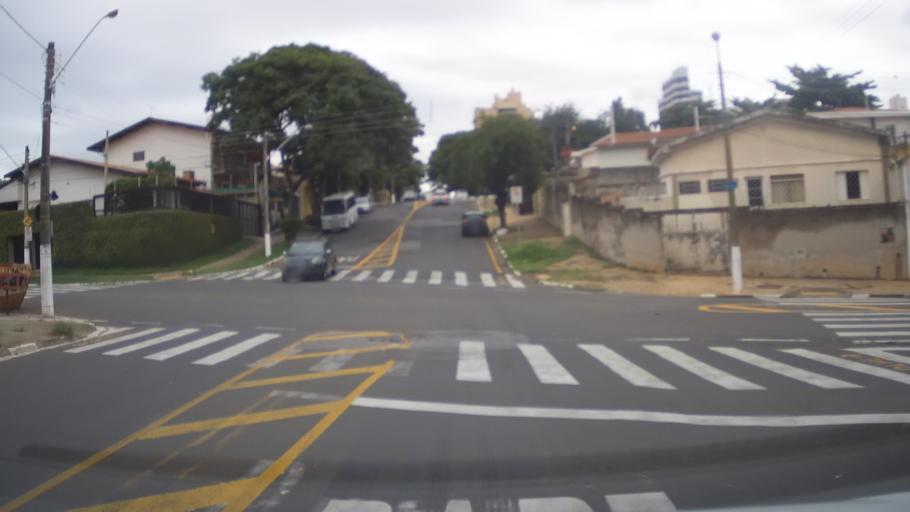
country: BR
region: Sao Paulo
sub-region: Campinas
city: Campinas
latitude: -22.9130
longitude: -47.0410
